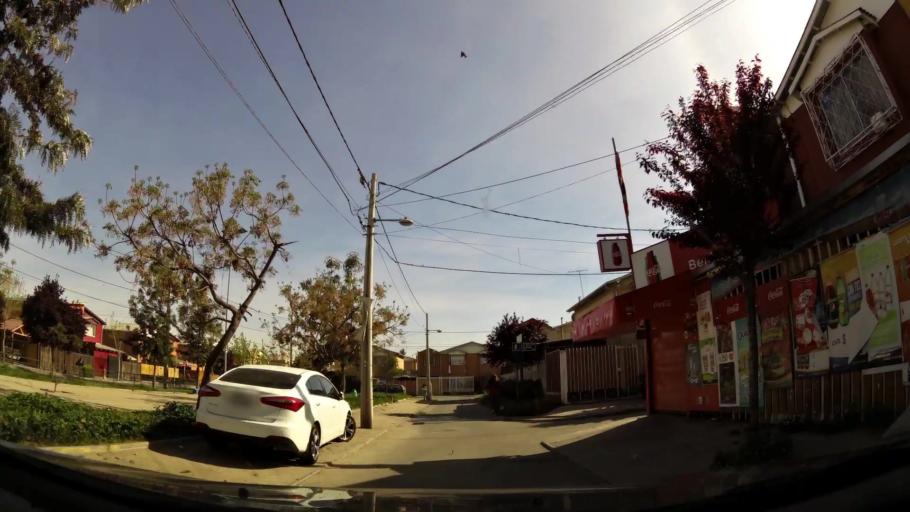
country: CL
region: Santiago Metropolitan
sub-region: Provincia de Cordillera
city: Puente Alto
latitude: -33.6105
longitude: -70.5985
